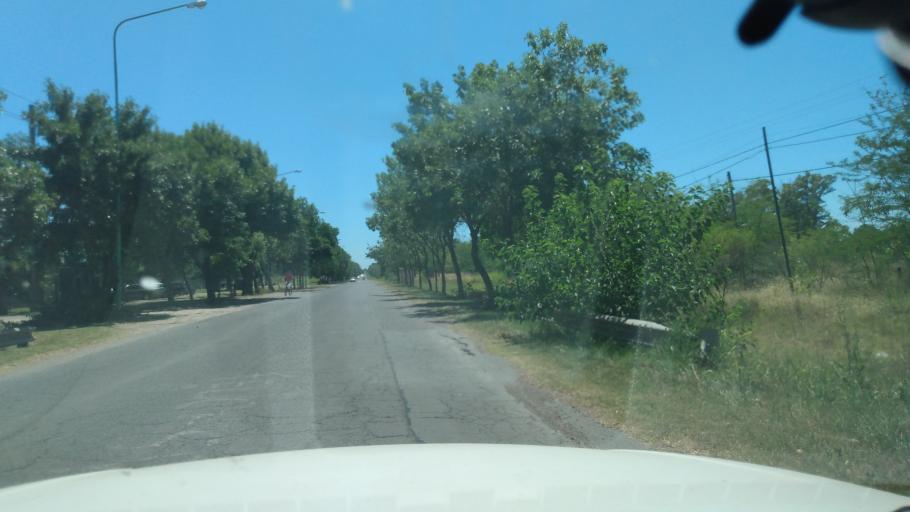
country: AR
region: Buenos Aires
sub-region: Partido de Lujan
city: Lujan
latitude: -34.5795
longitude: -59.1710
